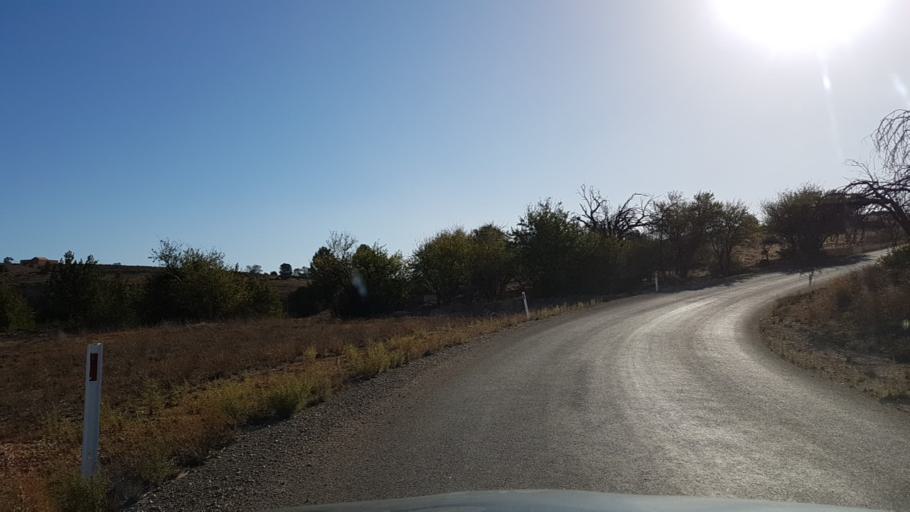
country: AU
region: South Australia
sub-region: Clare and Gilbert Valleys
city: Clare
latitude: -33.6768
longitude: 138.9282
